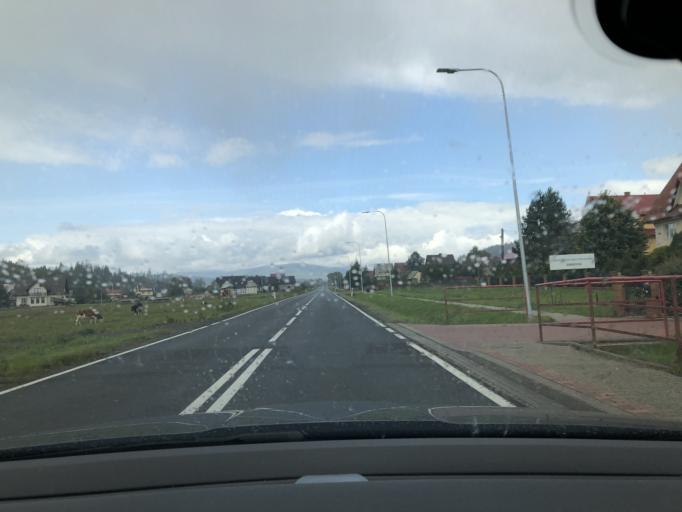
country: PL
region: Lesser Poland Voivodeship
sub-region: Powiat nowotarski
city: Zubrzyca Dolna
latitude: 49.5044
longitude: 19.6775
